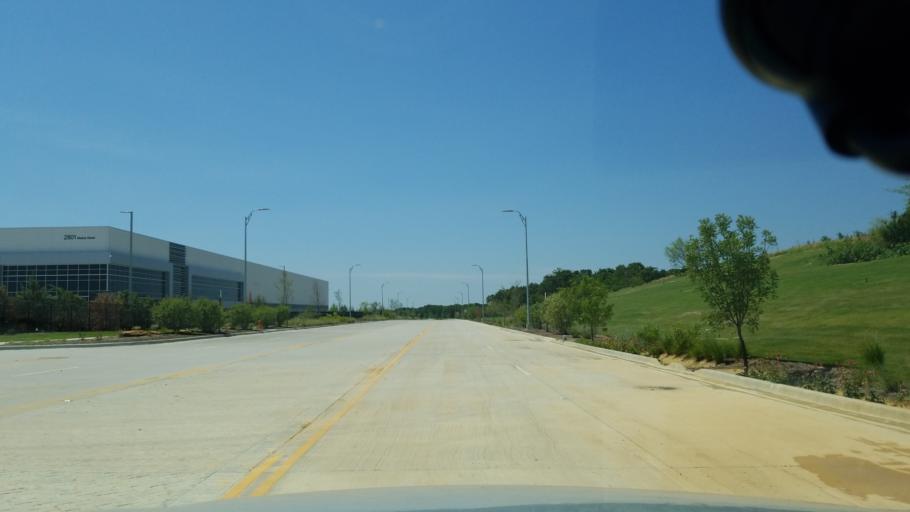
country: US
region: Texas
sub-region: Tarrant County
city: Euless
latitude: 32.8457
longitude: -97.0310
